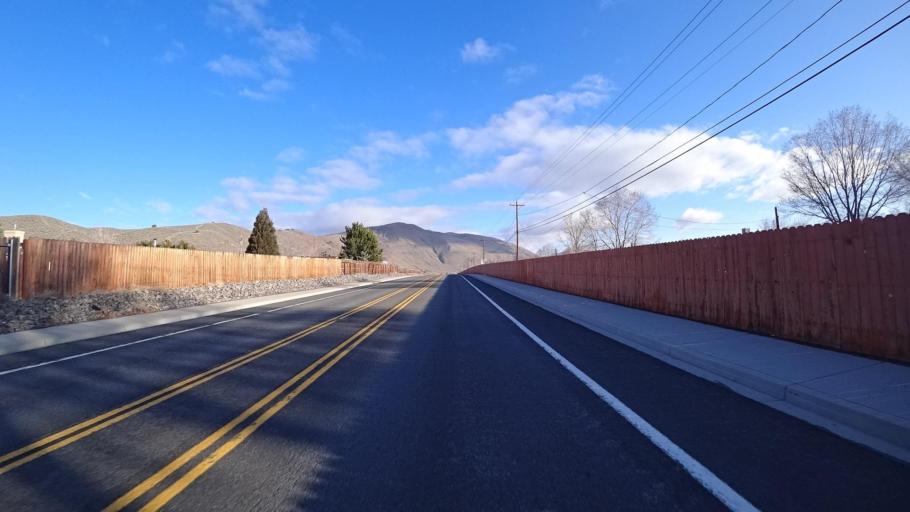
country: US
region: Nevada
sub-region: Washoe County
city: Cold Springs
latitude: 39.6820
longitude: -119.9784
